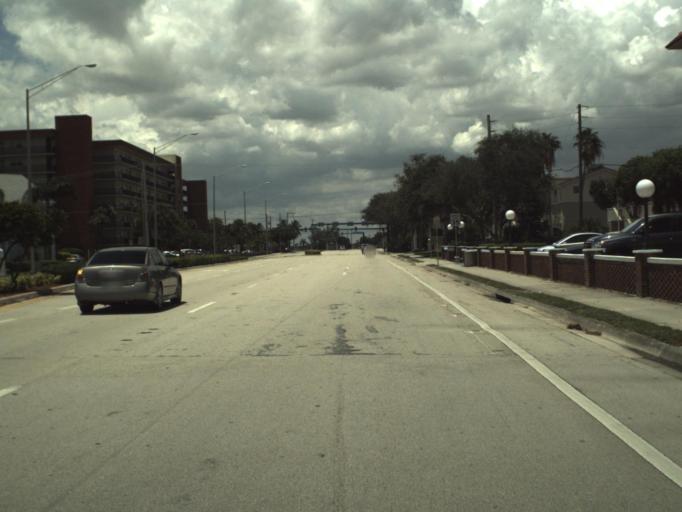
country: US
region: Florida
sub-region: Broward County
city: Kendall Green
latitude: 26.2502
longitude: -80.0974
